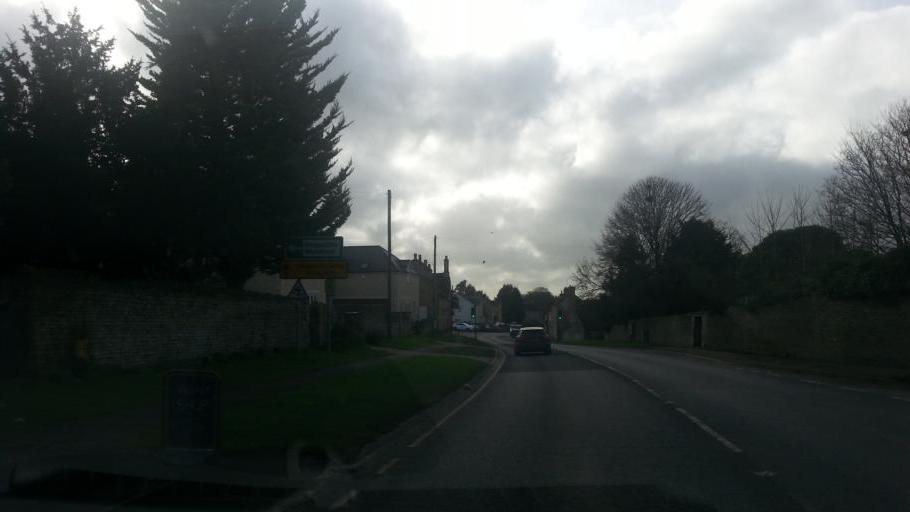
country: GB
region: England
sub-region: District of Rutland
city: Ketton
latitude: 52.6145
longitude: -0.5289
